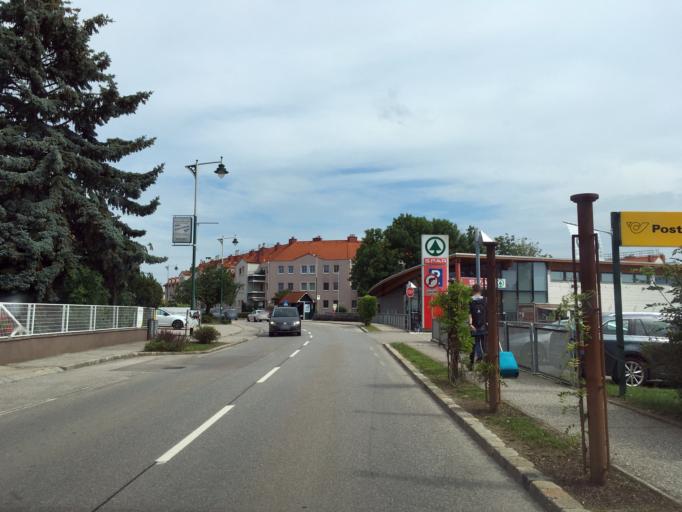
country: AT
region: Lower Austria
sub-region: Politischer Bezirk Wiener Neustadt
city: Bad Erlach
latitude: 47.7295
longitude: 16.2137
